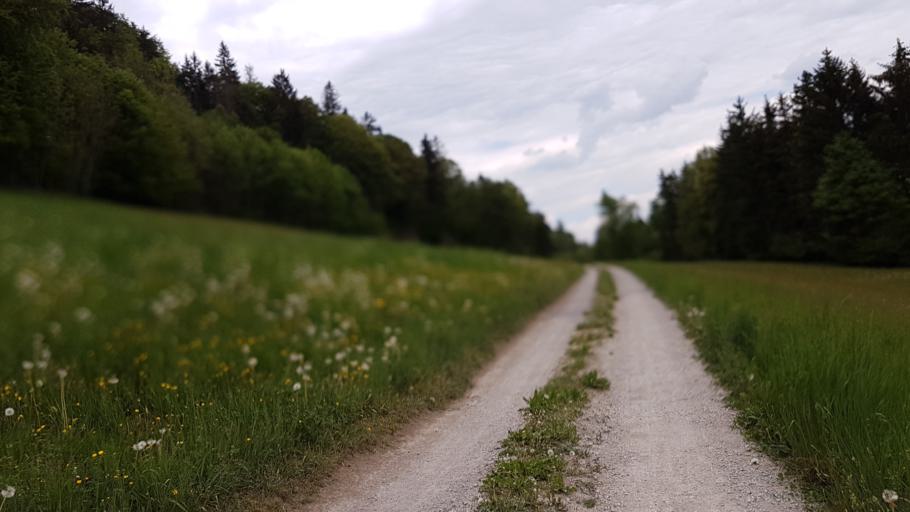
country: CH
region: Bern
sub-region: Bern-Mittelland District
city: Munsingen
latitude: 46.8576
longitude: 7.5506
